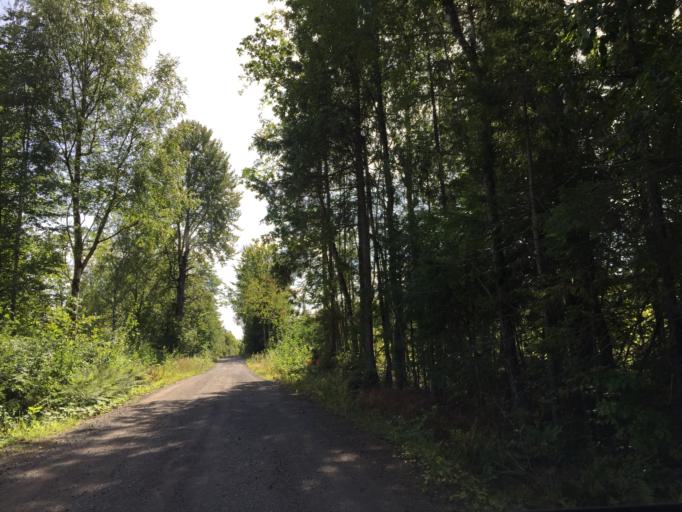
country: NO
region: Vestfold
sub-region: Hof
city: Hof
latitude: 59.4458
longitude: 10.1565
